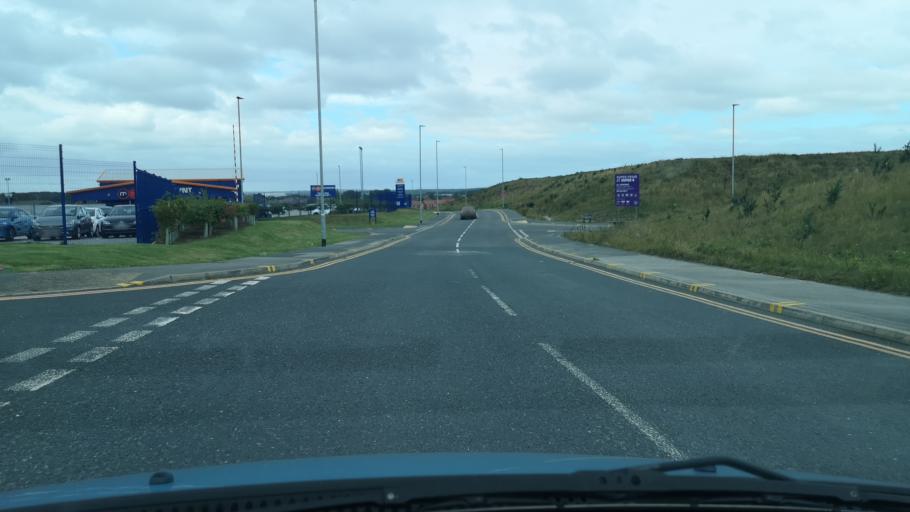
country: GB
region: England
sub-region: City and Borough of Wakefield
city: Castleford
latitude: 53.7068
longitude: -1.3501
